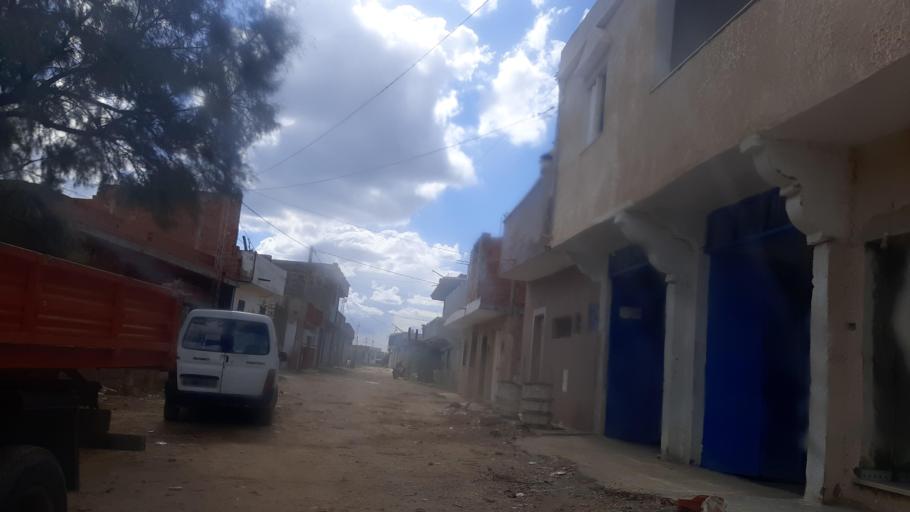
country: TN
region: Nabul
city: Korba
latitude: 36.5914
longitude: 10.8564
